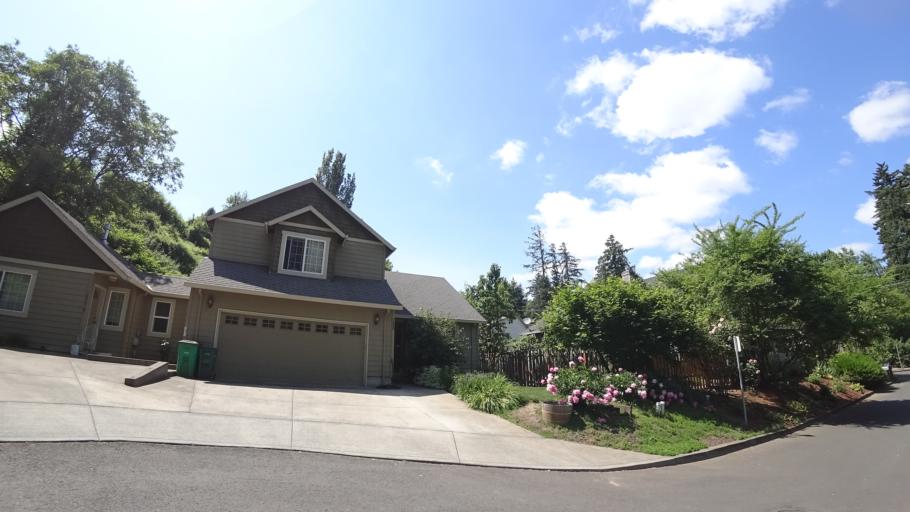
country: US
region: Oregon
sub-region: Washington County
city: Garden Home-Whitford
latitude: 45.4732
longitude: -122.7038
